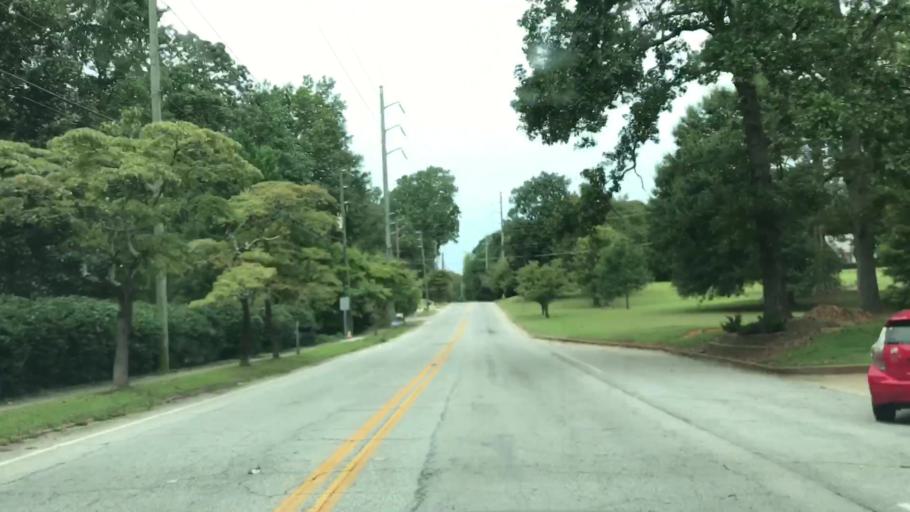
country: US
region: Georgia
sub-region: DeKalb County
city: Avondale Estates
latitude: 33.7663
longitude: -84.2815
